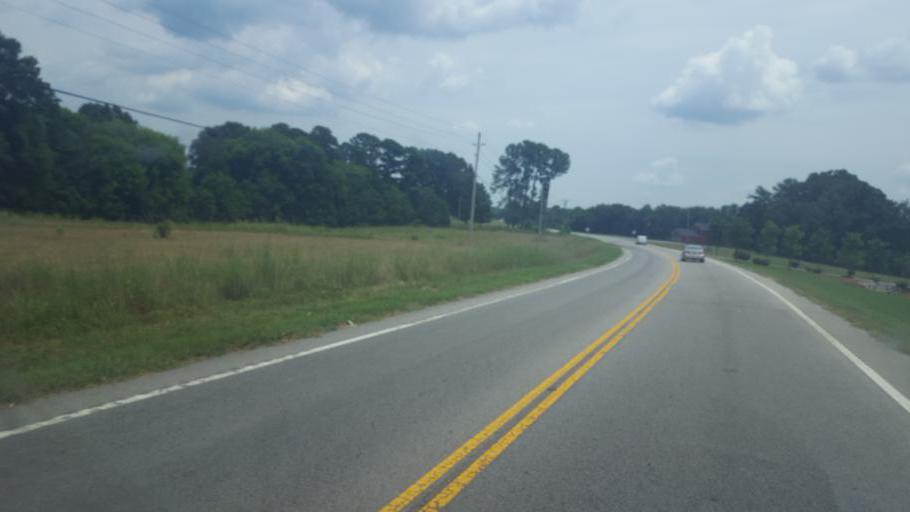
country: US
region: South Carolina
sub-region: York County
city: Newport
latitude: 34.9646
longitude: -81.1487
